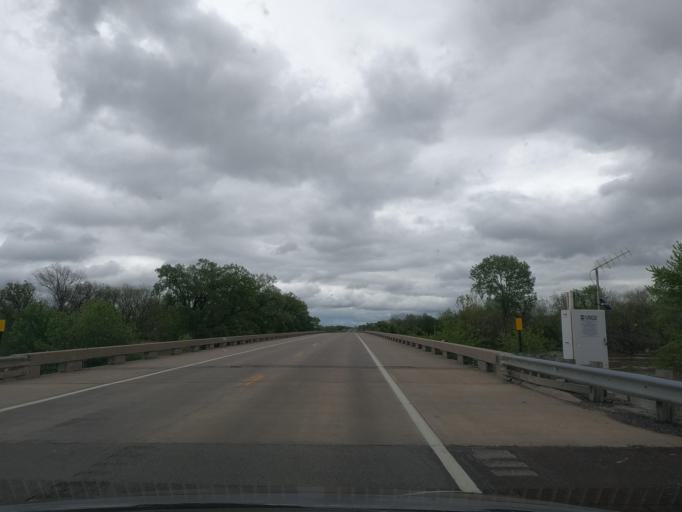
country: US
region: Kansas
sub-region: Labette County
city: Parsons
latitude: 37.3403
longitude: -95.1100
